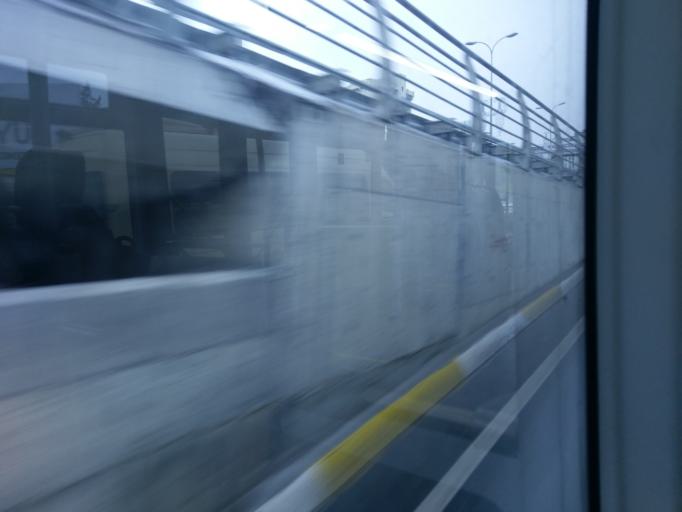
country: TR
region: Istanbul
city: Mahmutbey
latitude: 41.0335
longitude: 28.7700
